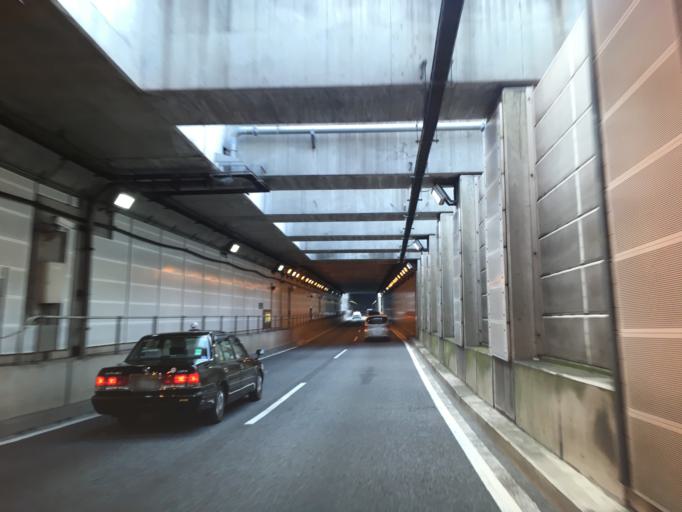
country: JP
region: Saitama
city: Wako
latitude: 35.7317
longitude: 139.6146
